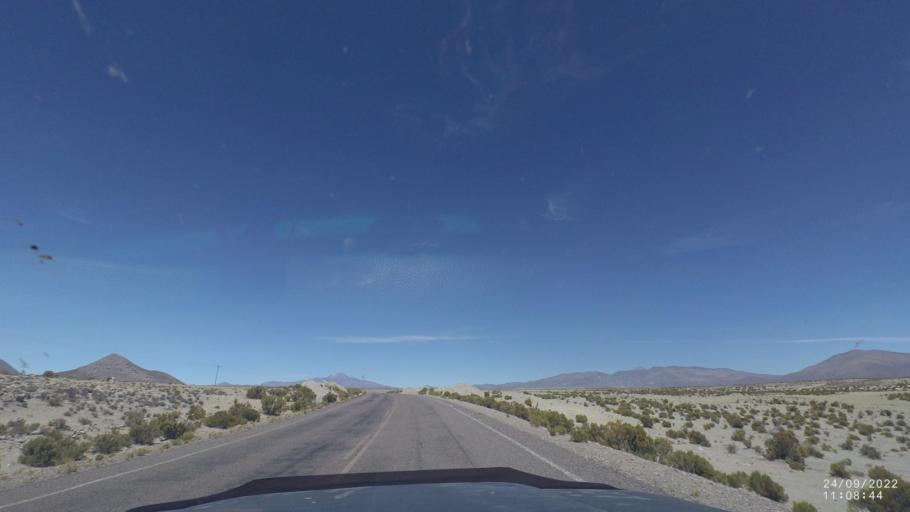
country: BO
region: Oruro
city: Challapata
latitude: -19.4881
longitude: -67.4446
